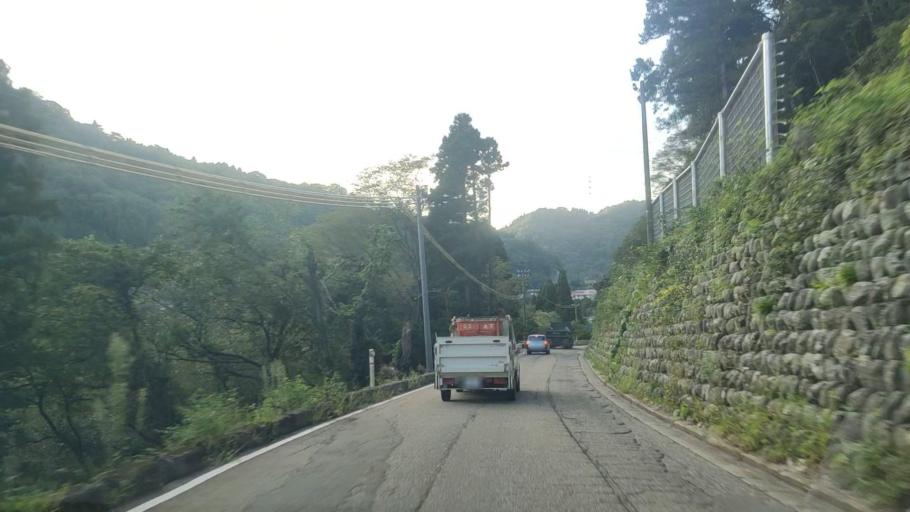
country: JP
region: Toyama
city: Nanto-shi
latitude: 36.5585
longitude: 137.0086
